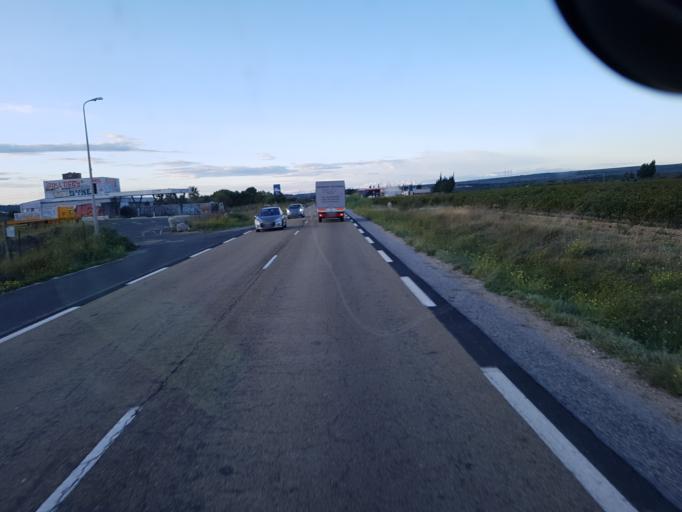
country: FR
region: Languedoc-Roussillon
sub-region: Departement de l'Aude
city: Leucate
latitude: 42.9426
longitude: 2.9894
